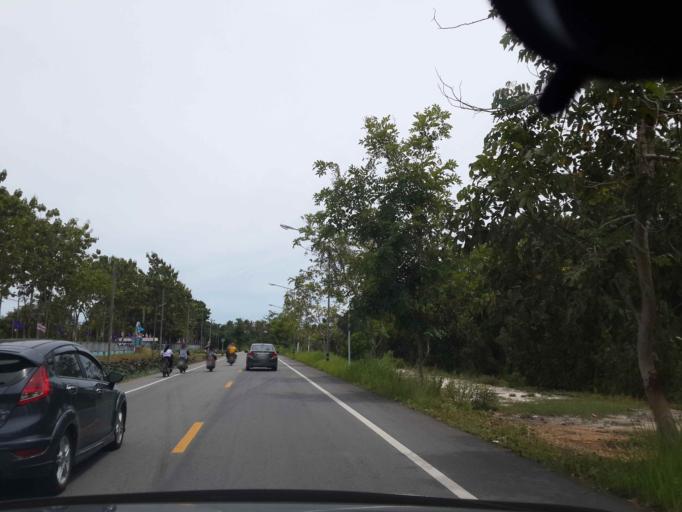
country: TH
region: Narathiwat
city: Narathiwat
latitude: 6.4403
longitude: 101.7923
